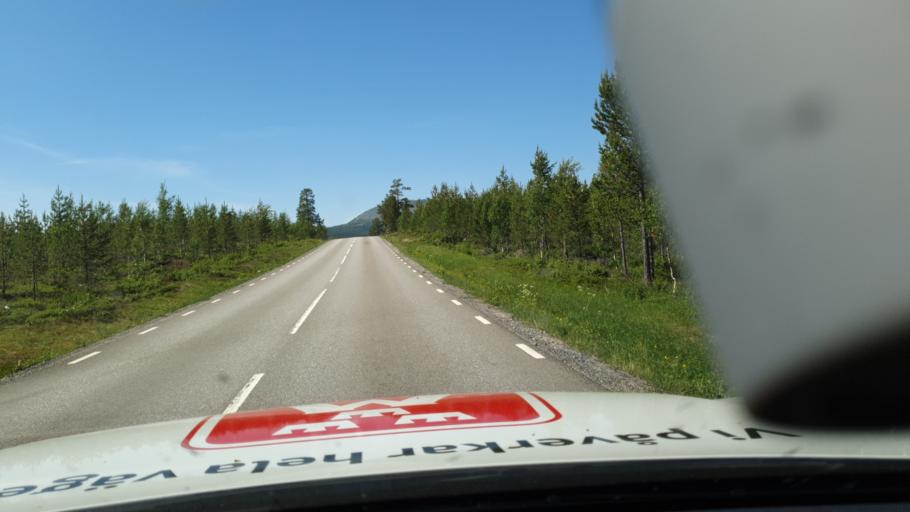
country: SE
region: Jaemtland
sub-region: Harjedalens Kommun
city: Sveg
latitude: 62.1046
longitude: 13.4278
